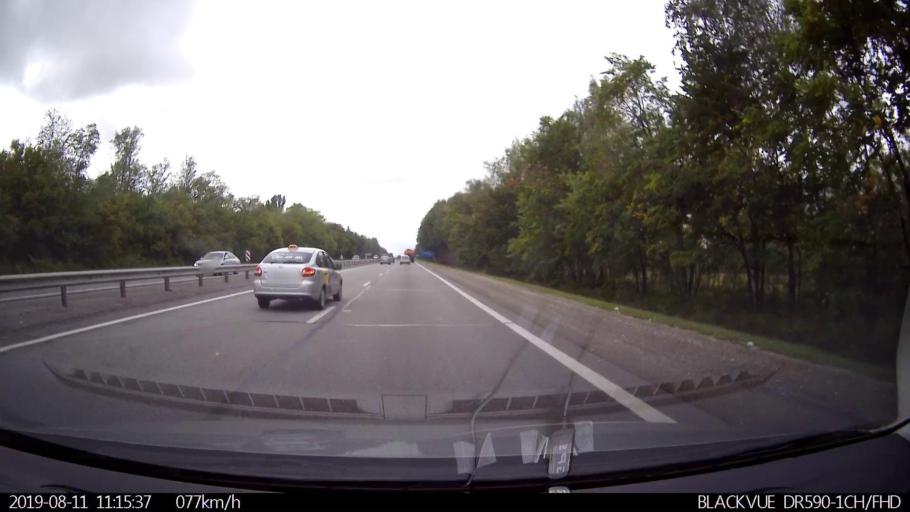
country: RU
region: Ulyanovsk
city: Novoul'yanovsk
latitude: 54.2014
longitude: 48.2890
